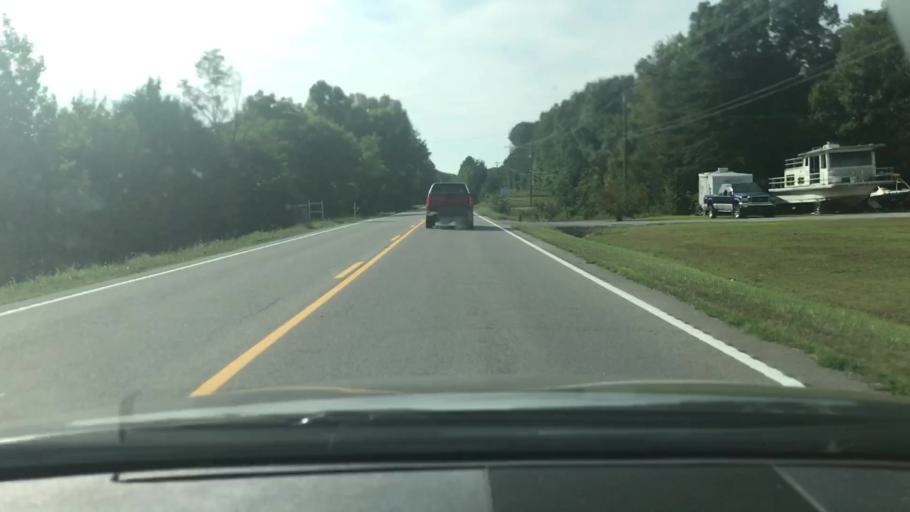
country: US
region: Tennessee
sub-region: Williamson County
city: Fairview
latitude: 36.0138
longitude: -87.1533
